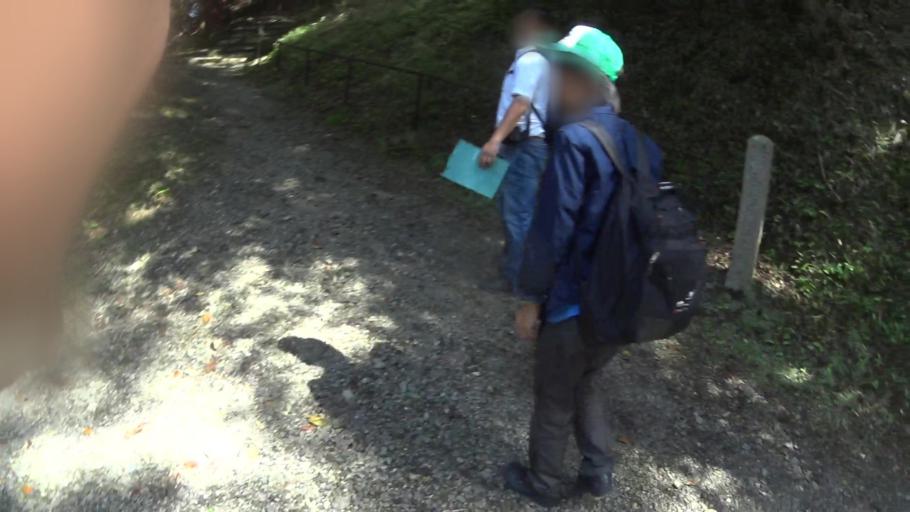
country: JP
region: Shiga Prefecture
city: Kitahama
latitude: 35.0991
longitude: 135.8545
